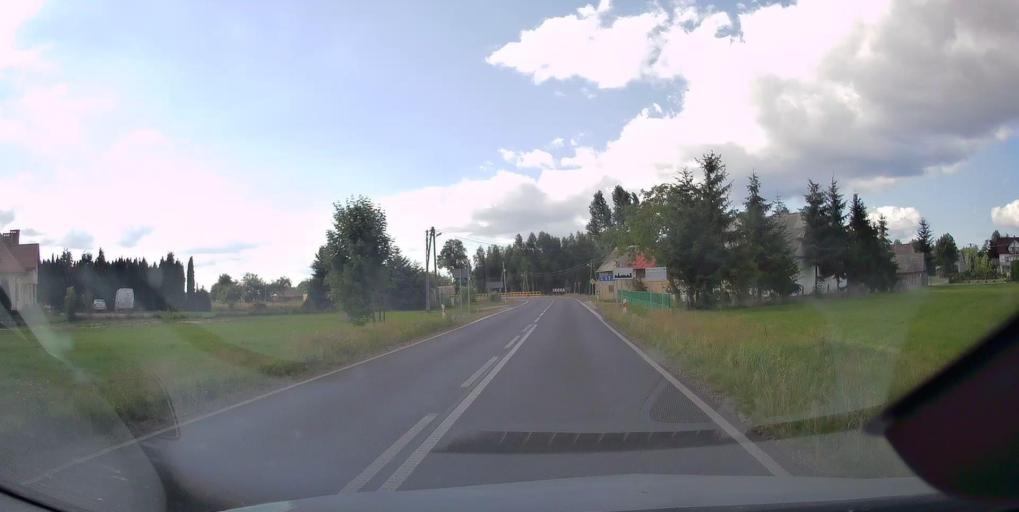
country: PL
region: Swietokrzyskie
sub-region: Powiat kielecki
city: Bodzentyn
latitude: 50.9297
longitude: 20.9799
